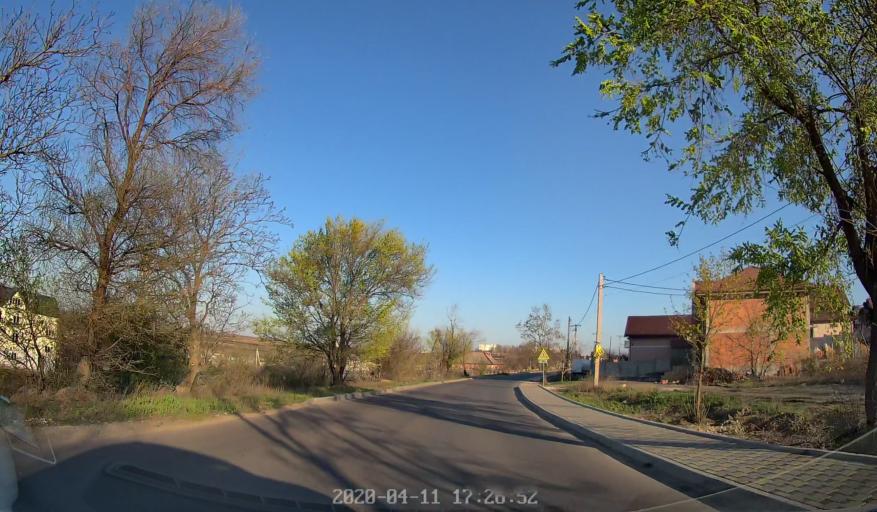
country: MD
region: Chisinau
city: Vatra
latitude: 47.0118
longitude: 28.7593
